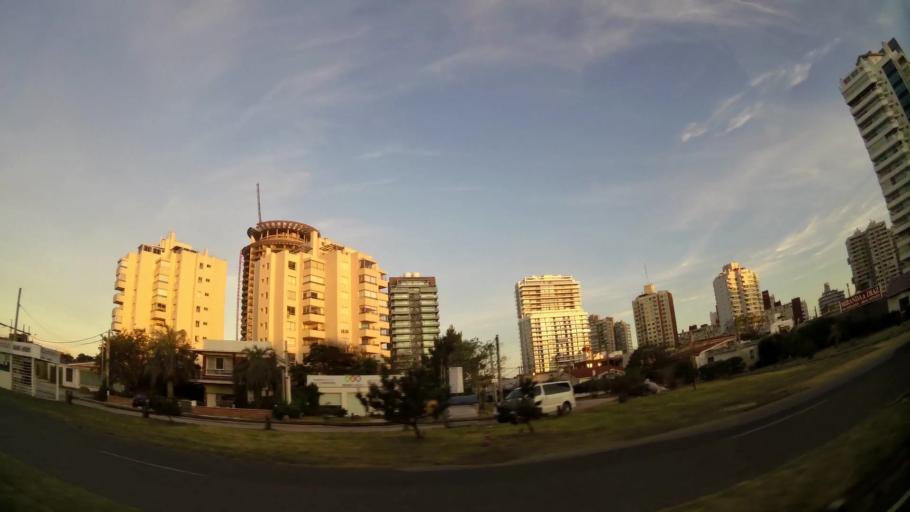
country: UY
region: Maldonado
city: Punta del Este
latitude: -34.9524
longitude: -54.9381
